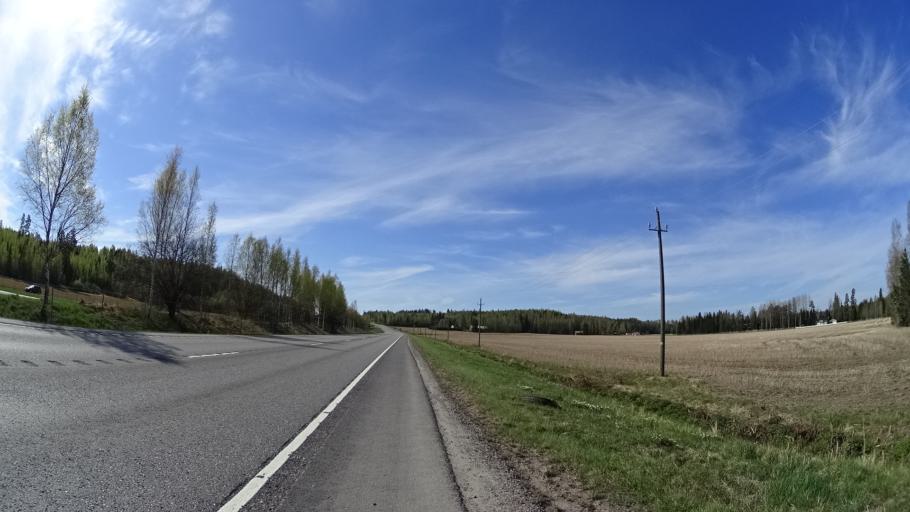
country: FI
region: Uusimaa
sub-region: Helsinki
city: Nurmijaervi
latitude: 60.4252
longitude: 24.8251
